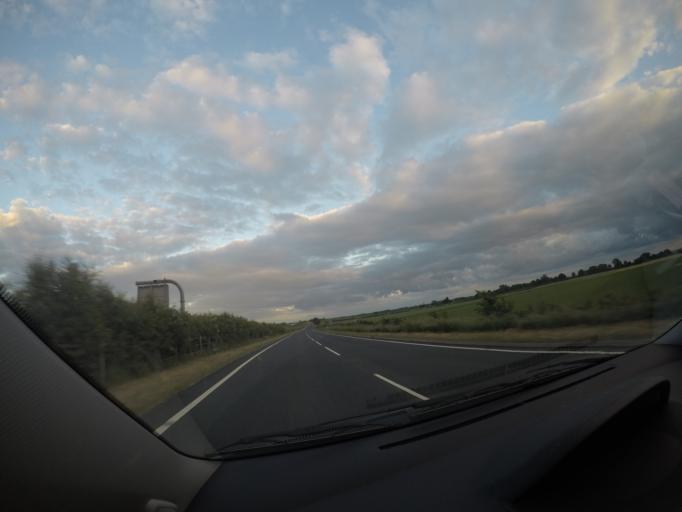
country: GB
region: England
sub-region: North Yorkshire
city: Bedale
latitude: 54.2678
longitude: -1.5222
